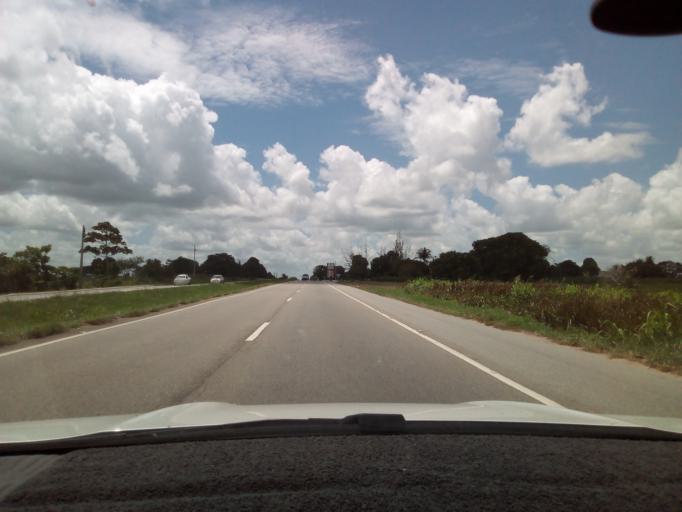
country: BR
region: Paraiba
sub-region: Pilar
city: Pilar
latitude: -7.1842
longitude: -35.2991
